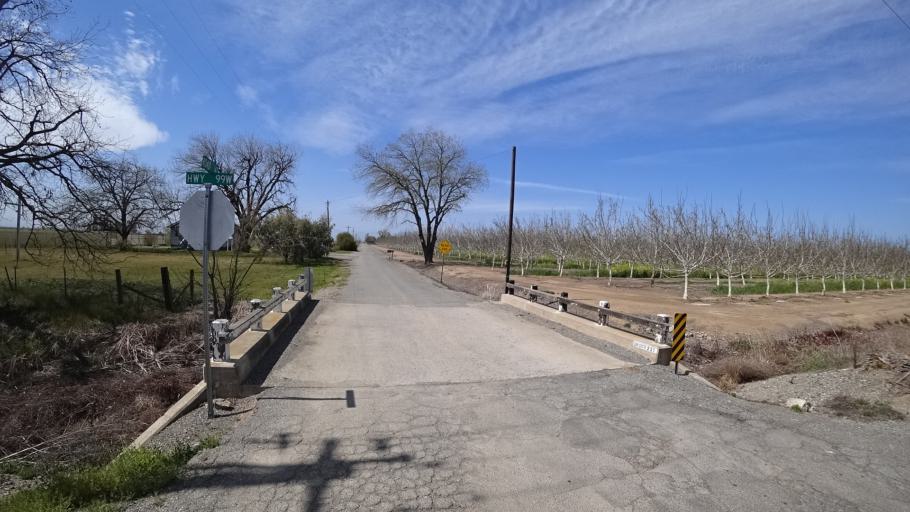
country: US
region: California
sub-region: Glenn County
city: Willows
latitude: 39.5733
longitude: -122.1940
